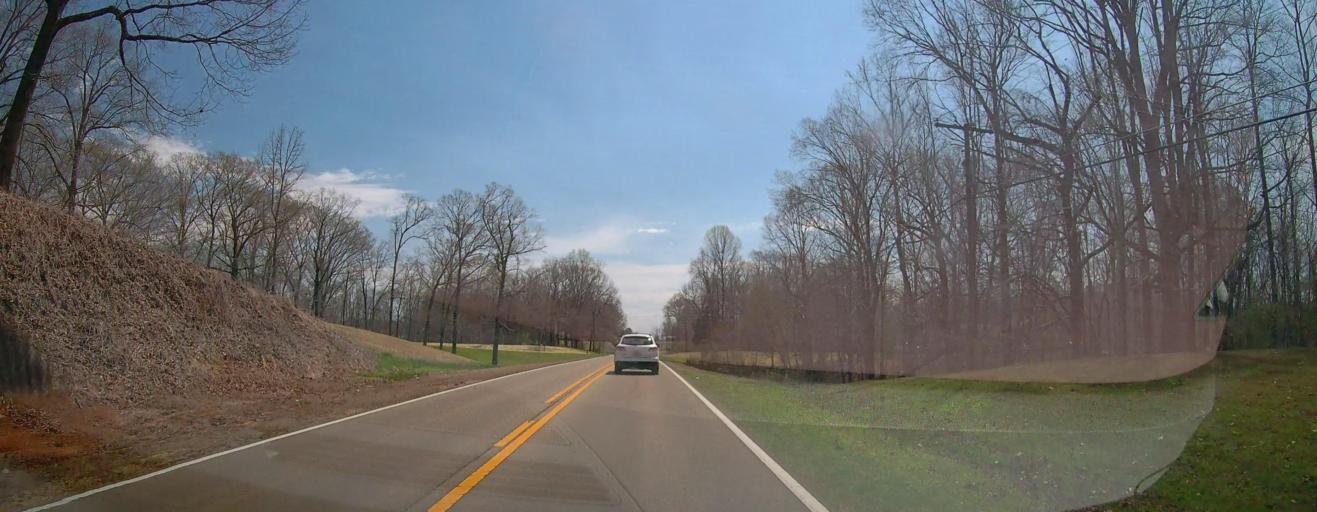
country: US
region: Mississippi
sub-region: Union County
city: New Albany
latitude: 34.4410
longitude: -88.9615
